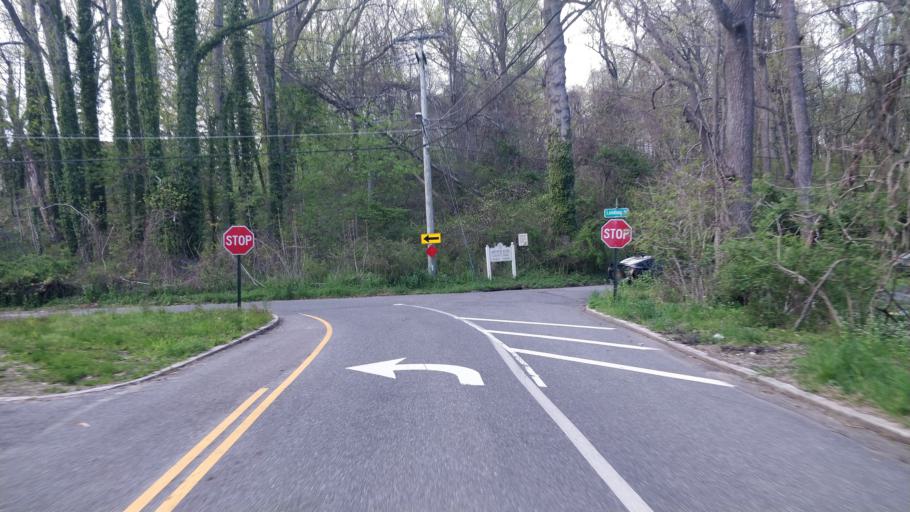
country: US
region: New York
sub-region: Suffolk County
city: Nissequogue
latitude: 40.8908
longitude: -73.2163
